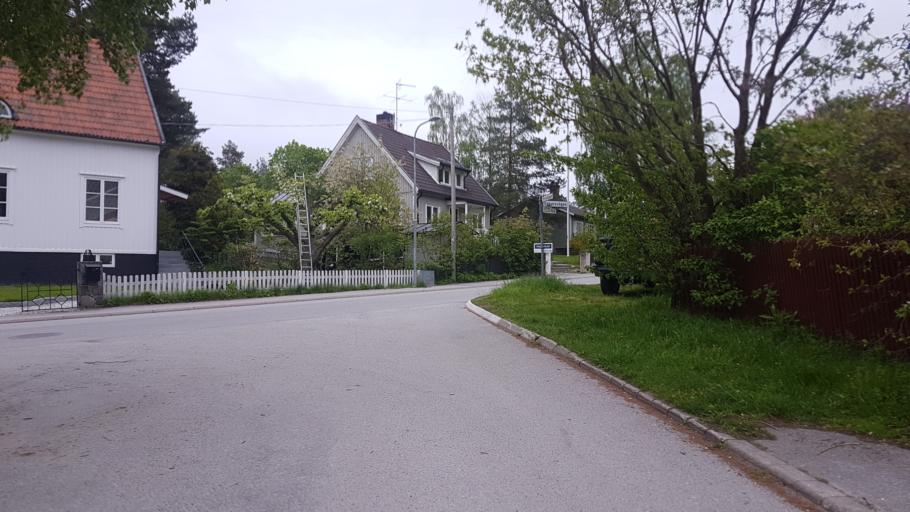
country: SE
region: Stockholm
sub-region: Lidingo
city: Lidingoe
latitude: 59.3570
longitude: 18.1424
